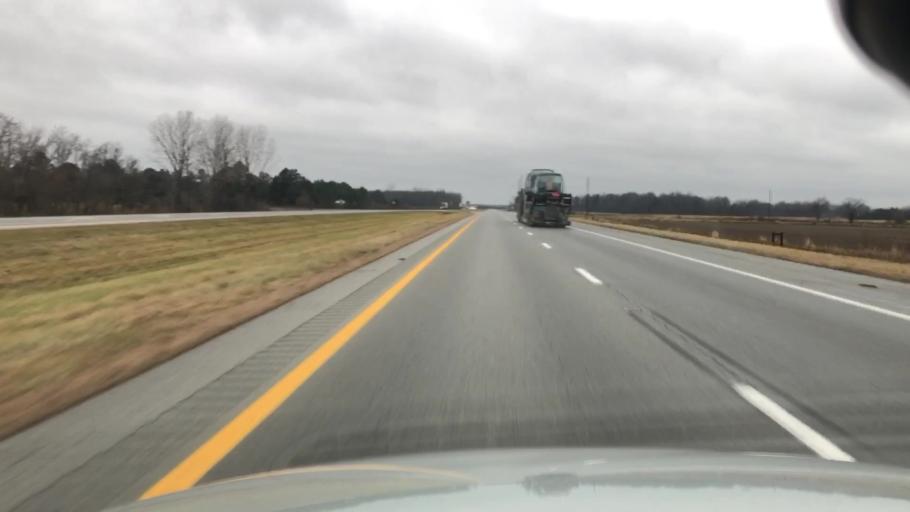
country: US
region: Ohio
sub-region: Allen County
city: Elida
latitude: 40.8293
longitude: -84.1446
